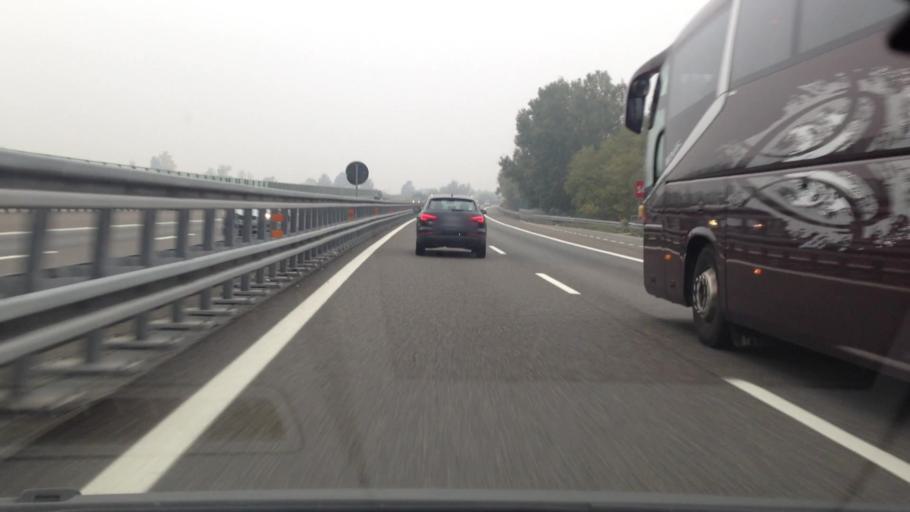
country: IT
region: Piedmont
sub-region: Provincia di Asti
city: Rocca d'Arazzo
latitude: 44.9094
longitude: 8.2807
